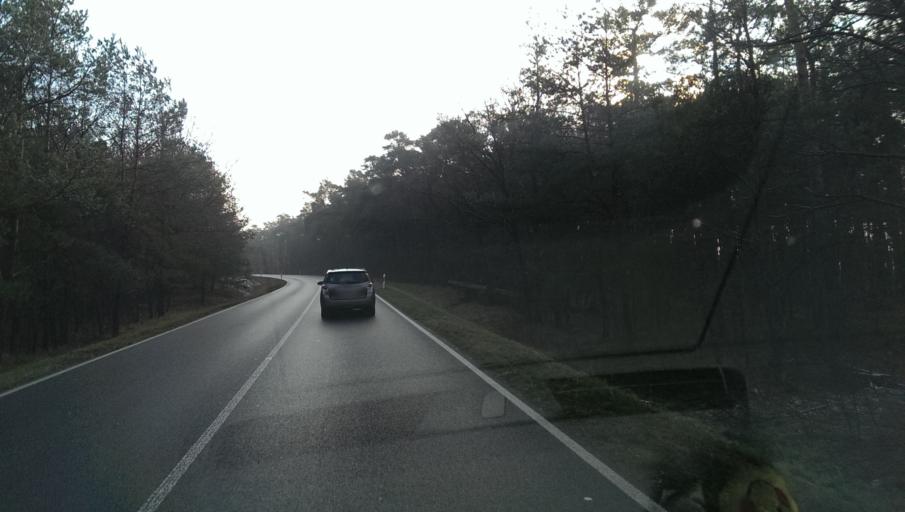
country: DE
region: Brandenburg
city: Herzberg
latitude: 51.7294
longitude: 13.2206
